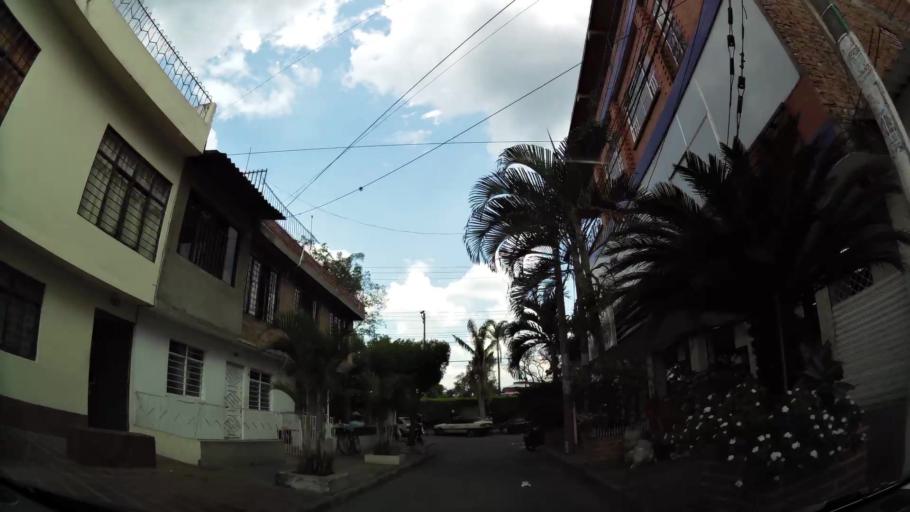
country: CO
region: Valle del Cauca
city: Cali
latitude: 3.4861
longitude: -76.4992
